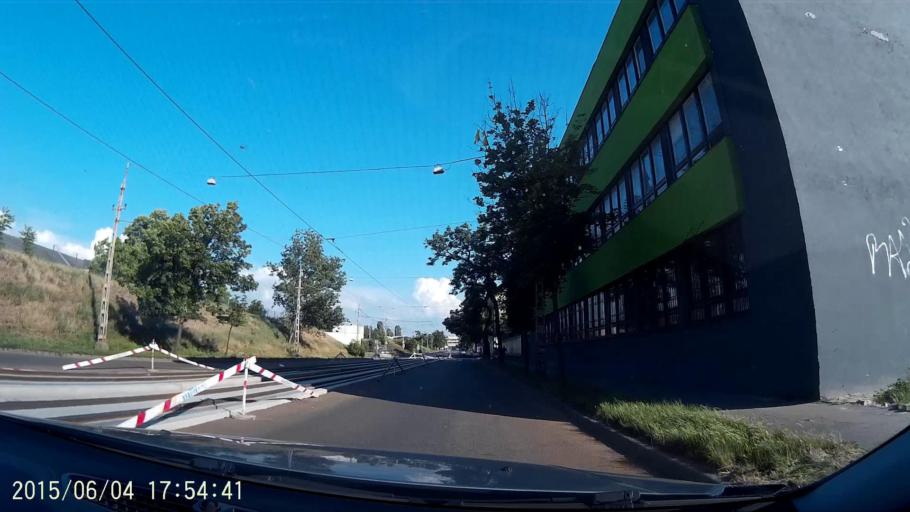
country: HU
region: Budapest
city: Budapest IX. keruelet
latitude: 47.4643
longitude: 19.0829
